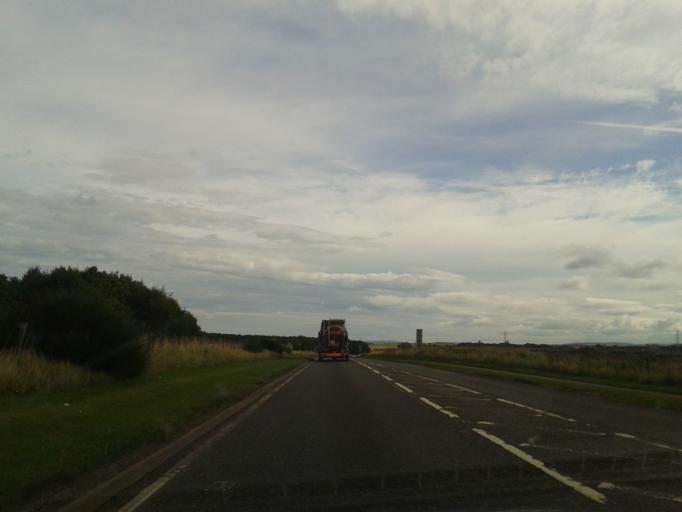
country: GB
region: Scotland
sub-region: Highland
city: Nairn
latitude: 57.5827
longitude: -3.8470
